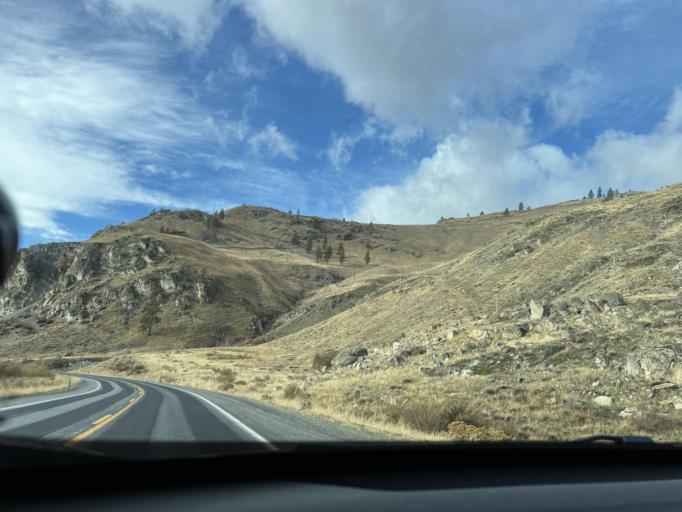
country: US
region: Washington
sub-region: Chelan County
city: Chelan
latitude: 47.8602
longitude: -119.9541
